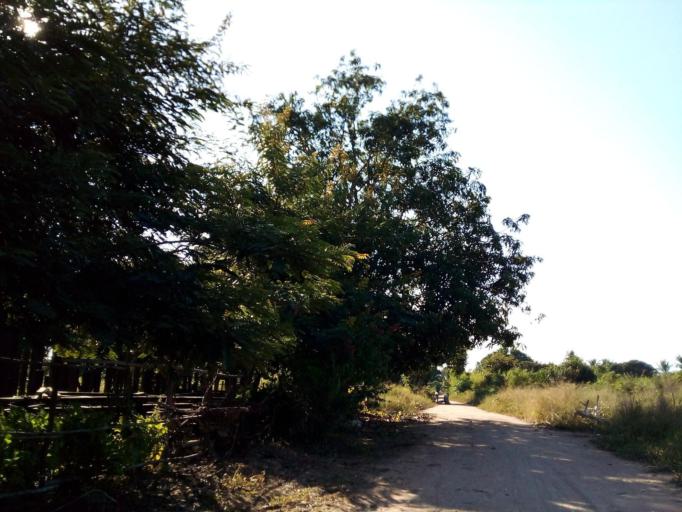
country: MZ
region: Zambezia
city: Quelimane
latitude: -17.5200
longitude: 36.6865
